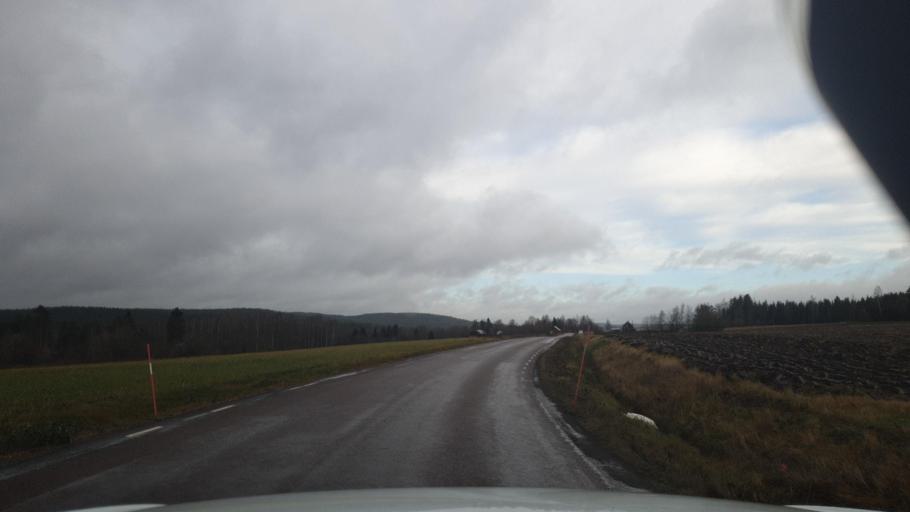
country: SE
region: Vaermland
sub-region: Eda Kommun
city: Charlottenberg
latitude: 59.7535
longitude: 12.1576
